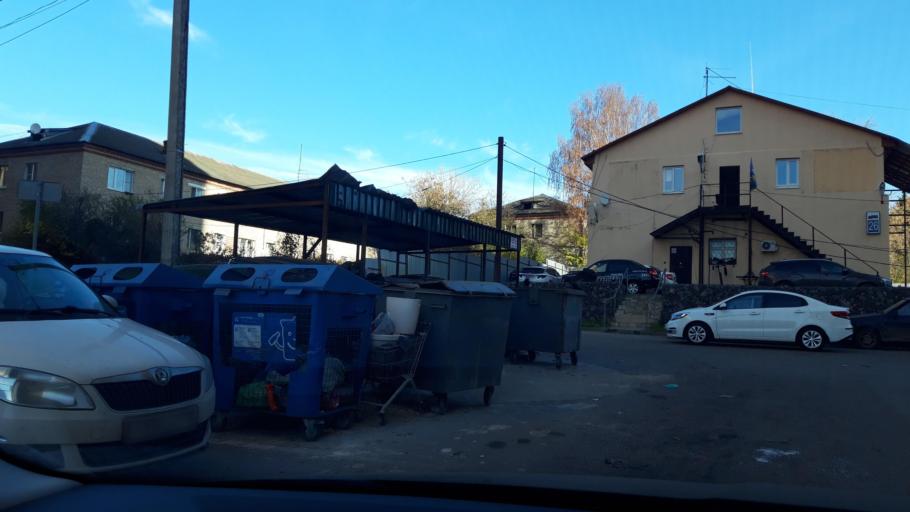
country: RU
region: Moskovskaya
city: Povarovo
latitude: 56.0828
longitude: 37.0477
